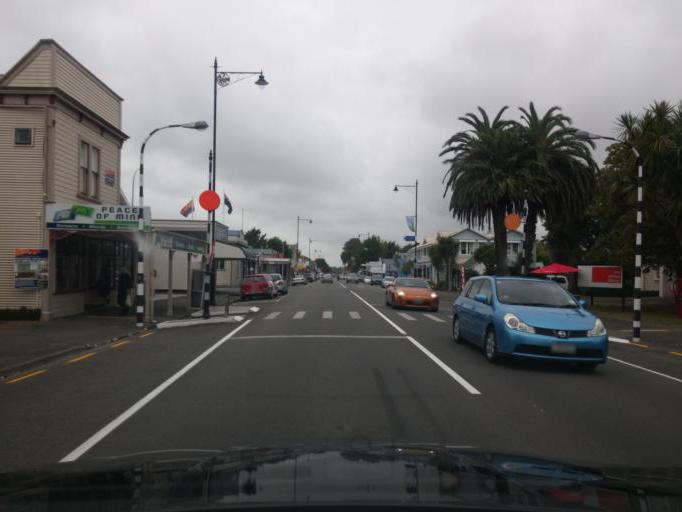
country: NZ
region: Wellington
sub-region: Masterton District
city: Masterton
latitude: -41.0814
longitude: 175.4592
